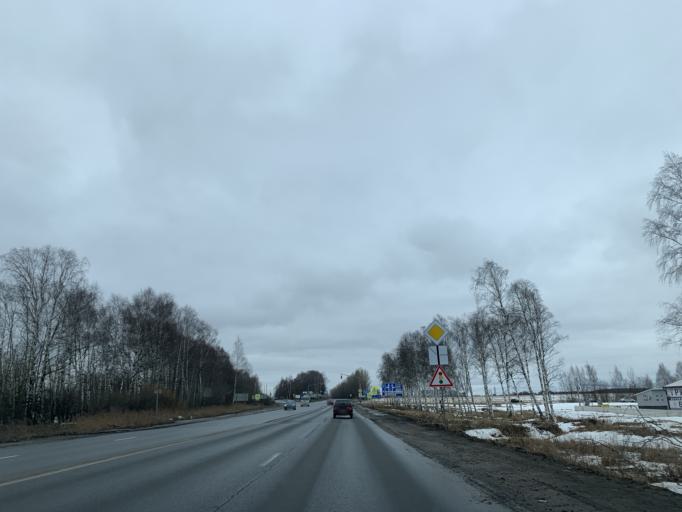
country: RU
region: Jaroslavl
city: Yaroslavl
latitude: 57.7315
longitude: 39.7389
